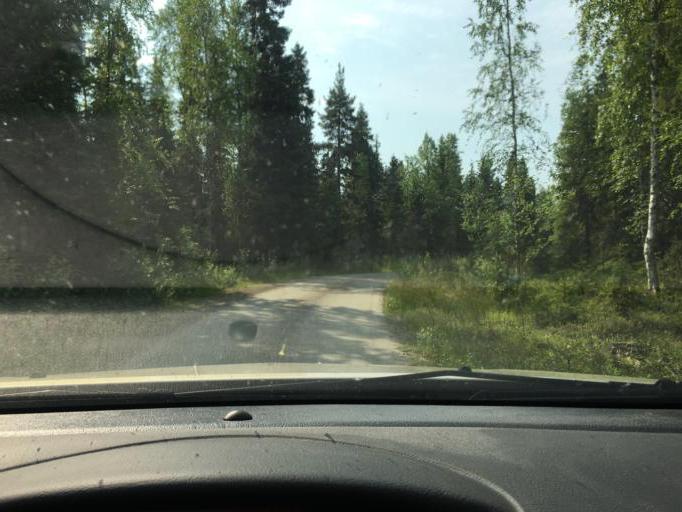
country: SE
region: Norrbotten
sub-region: Kalix Kommun
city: Rolfs
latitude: 65.7601
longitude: 22.9947
